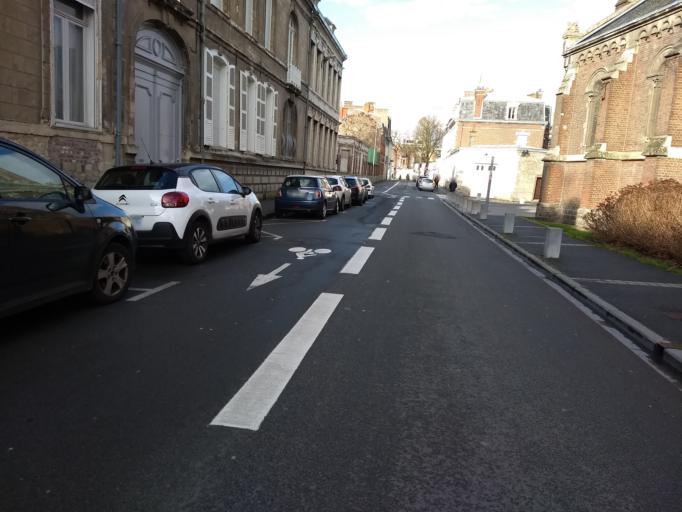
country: FR
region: Nord-Pas-de-Calais
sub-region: Departement du Pas-de-Calais
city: Arras
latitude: 50.2892
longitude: 2.7697
